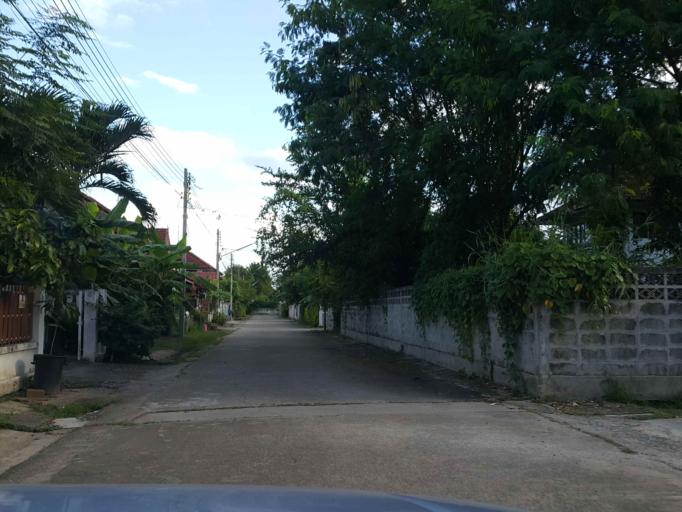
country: TH
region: Chiang Mai
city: San Sai
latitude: 18.9254
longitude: 98.9802
